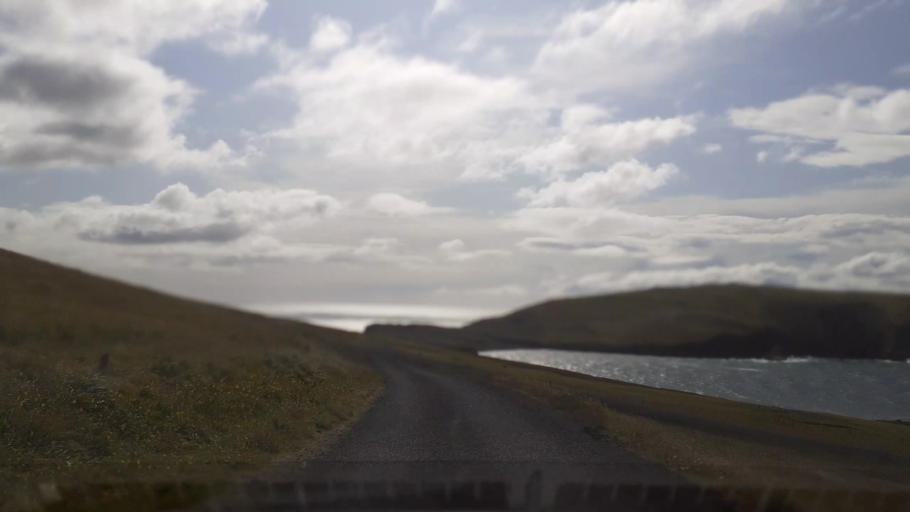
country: IS
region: South
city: Vestmannaeyjar
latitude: 63.4140
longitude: -20.2806
